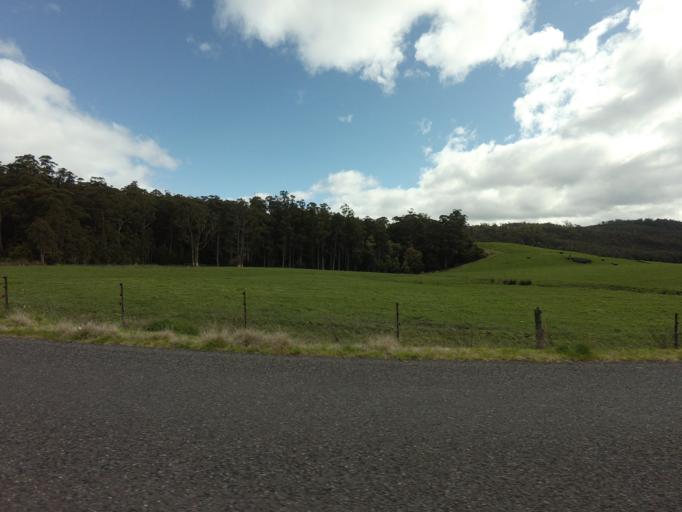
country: AU
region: Tasmania
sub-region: Huon Valley
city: Geeveston
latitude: -43.1941
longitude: 146.9393
